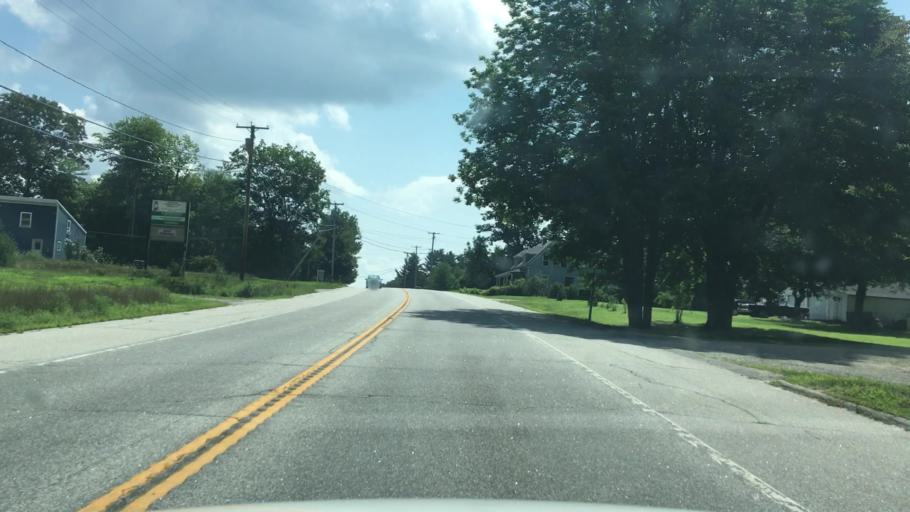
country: US
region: Maine
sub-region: Cumberland County
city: Raymond
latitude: 43.9283
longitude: -70.5355
